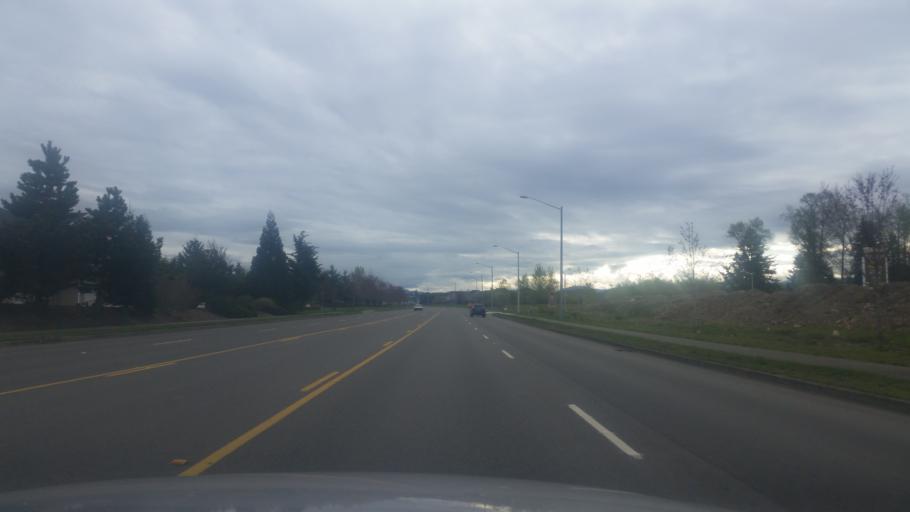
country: US
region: Washington
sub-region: Pierce County
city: South Hill
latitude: 47.0991
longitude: -122.2596
